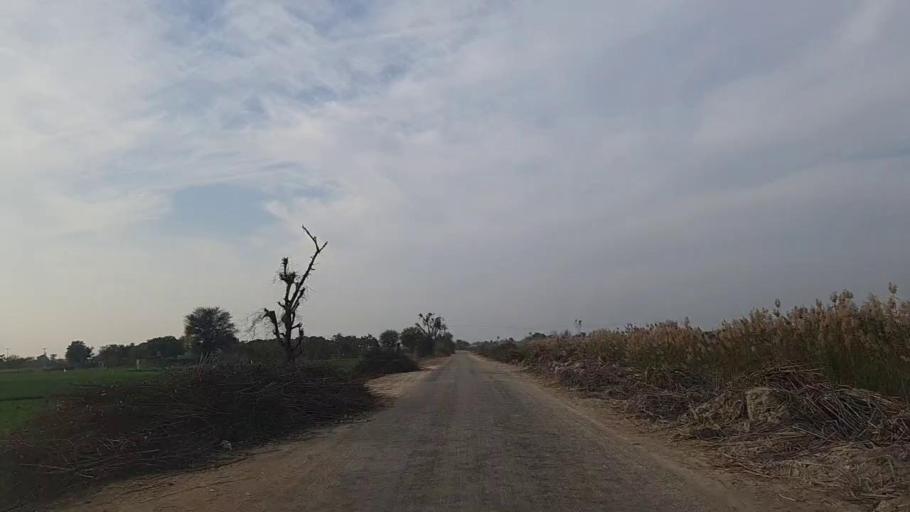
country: PK
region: Sindh
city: Daur
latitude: 26.5008
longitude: 68.4447
